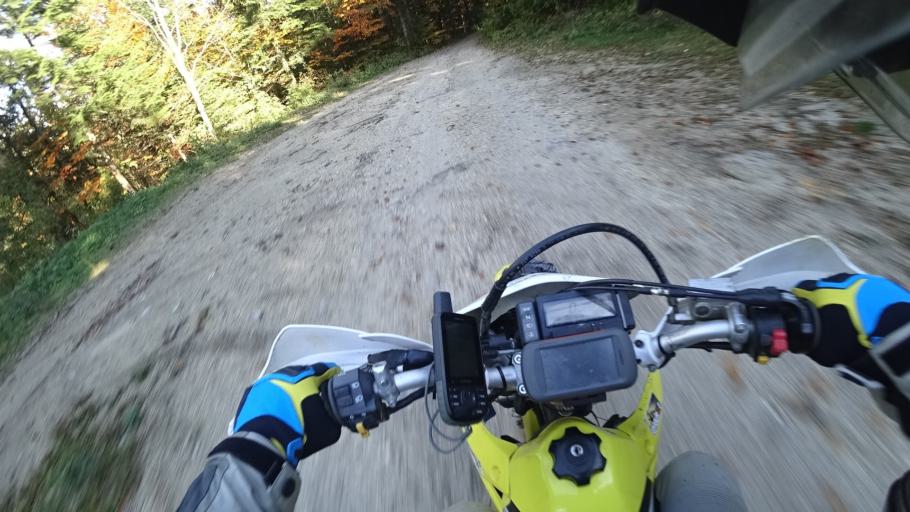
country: HR
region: Karlovacka
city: Plaski
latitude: 45.0416
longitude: 15.3592
